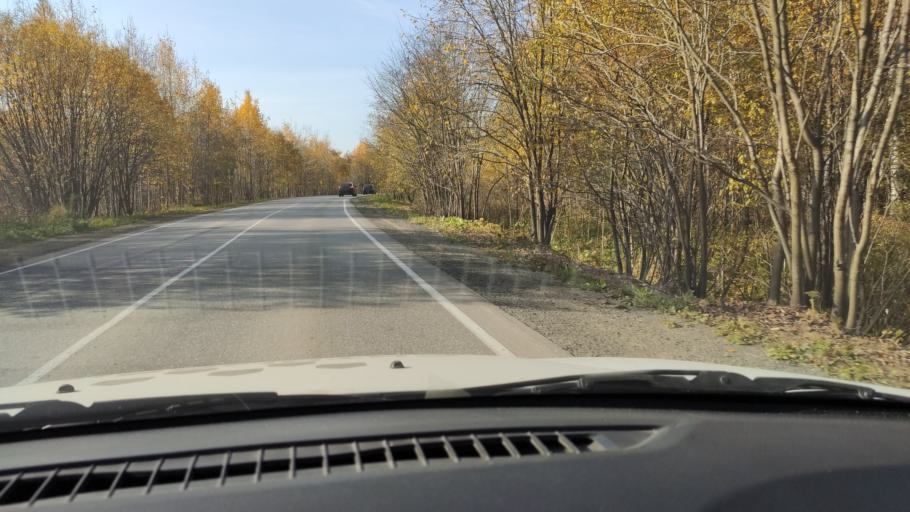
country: RU
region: Perm
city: Novyye Lyady
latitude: 58.0217
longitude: 56.6449
